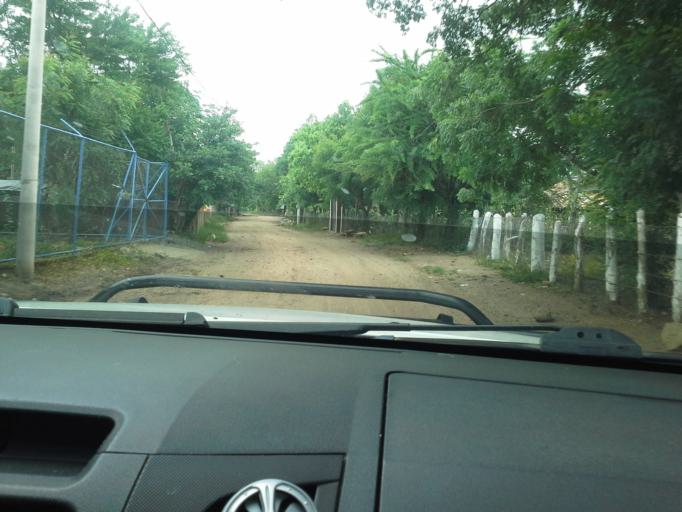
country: NI
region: Matagalpa
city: Ciudad Dario
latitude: 12.8341
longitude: -86.2137
